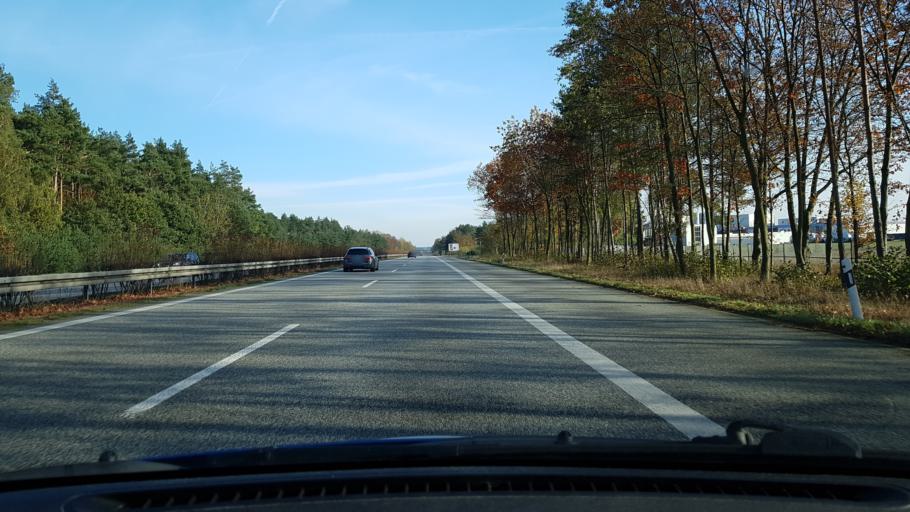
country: DE
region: Mecklenburg-Vorpommern
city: Zarrentin
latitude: 53.5086
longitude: 10.9875
